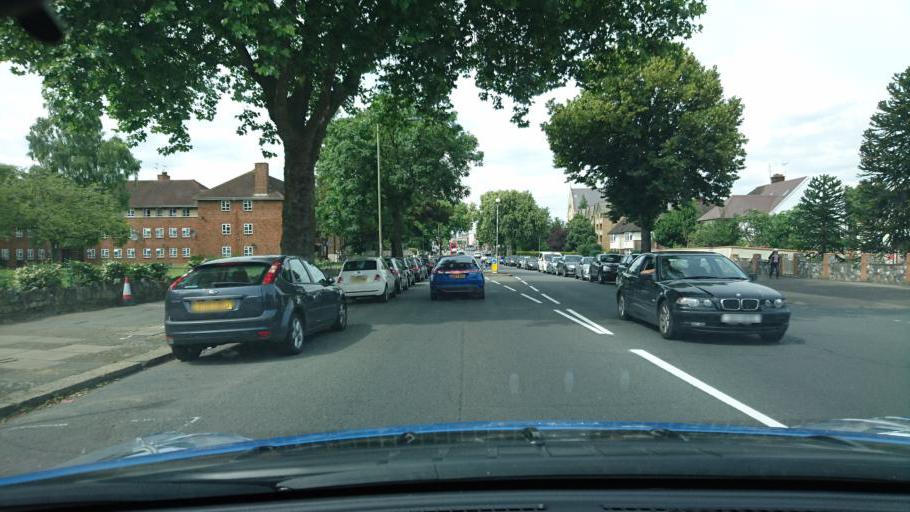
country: GB
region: England
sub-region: Greater London
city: Hendon
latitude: 51.6092
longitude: -0.1753
